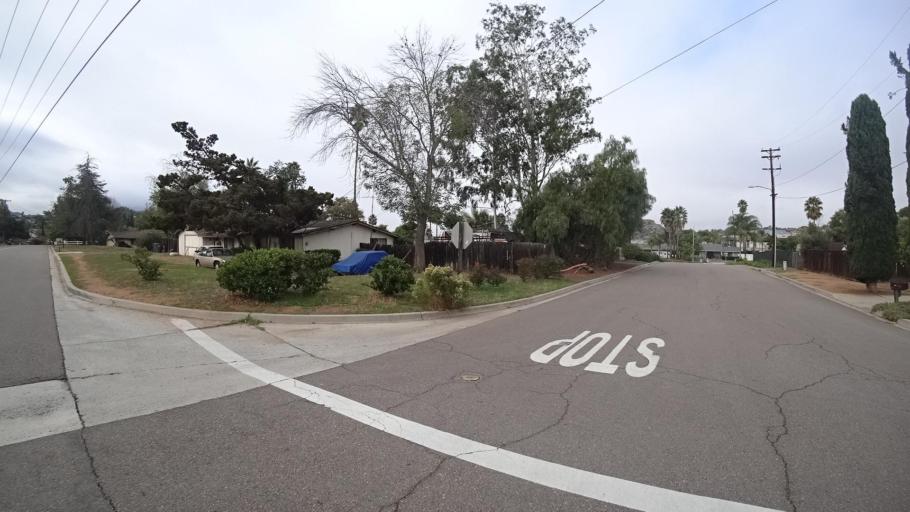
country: US
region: California
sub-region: San Diego County
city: Rancho San Diego
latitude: 32.7601
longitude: -116.9177
